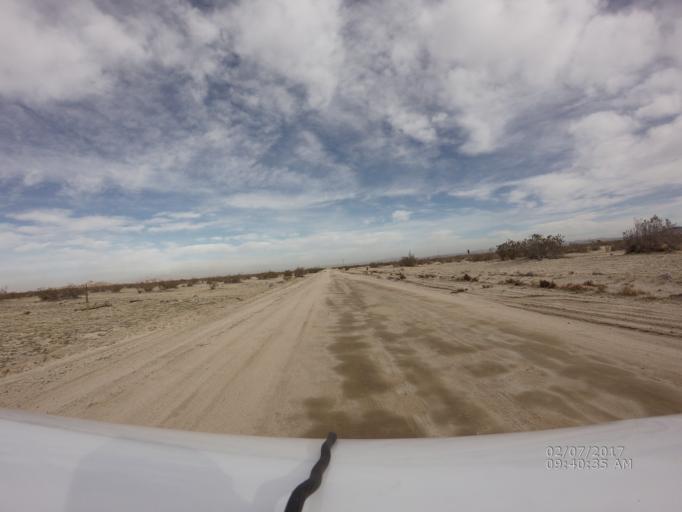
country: US
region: California
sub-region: Los Angeles County
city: Lake Los Angeles
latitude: 34.5618
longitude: -117.7114
